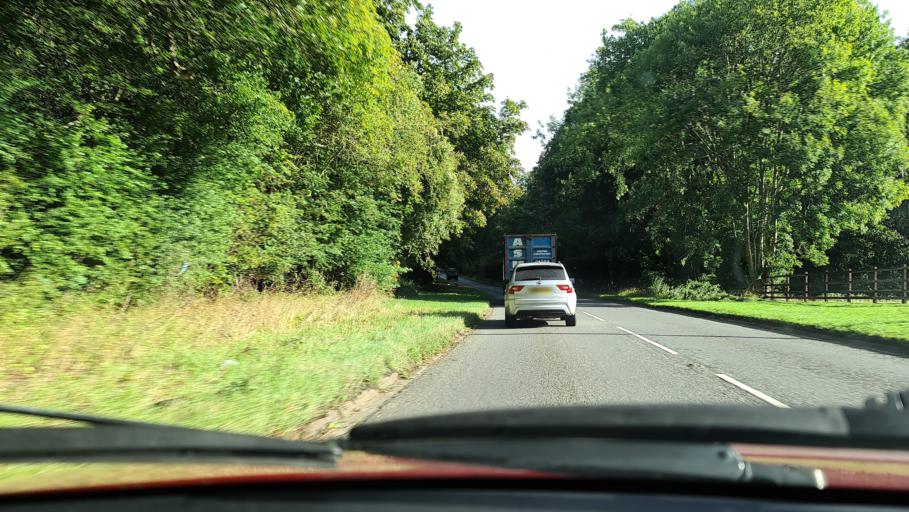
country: GB
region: England
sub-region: Buckinghamshire
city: Amersham
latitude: 51.6468
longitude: -0.6181
